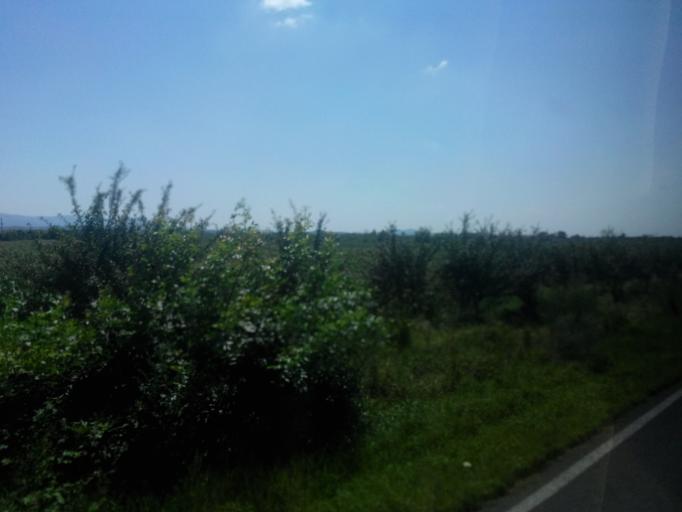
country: RO
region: Timis
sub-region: Comuna Margina
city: Margina
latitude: 45.8590
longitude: 22.2596
